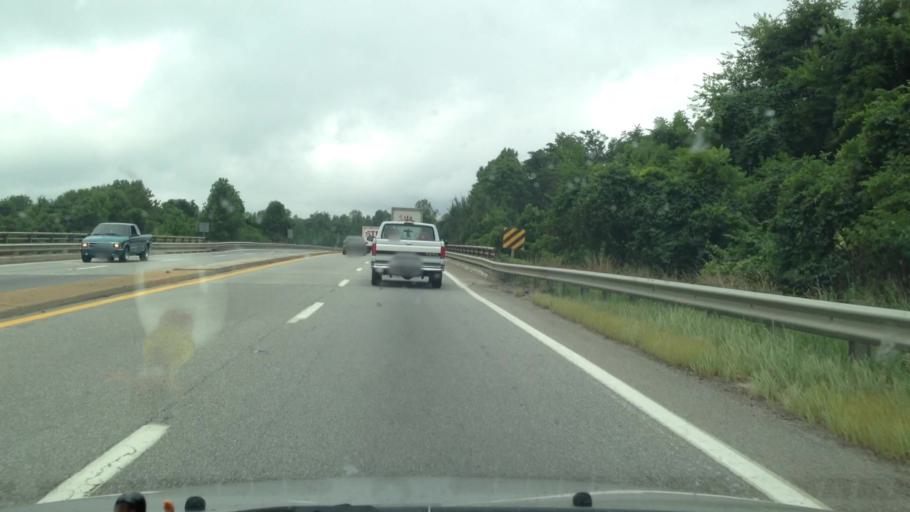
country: US
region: Virginia
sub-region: Henry County
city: Chatmoss
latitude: 36.5833
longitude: -79.8624
